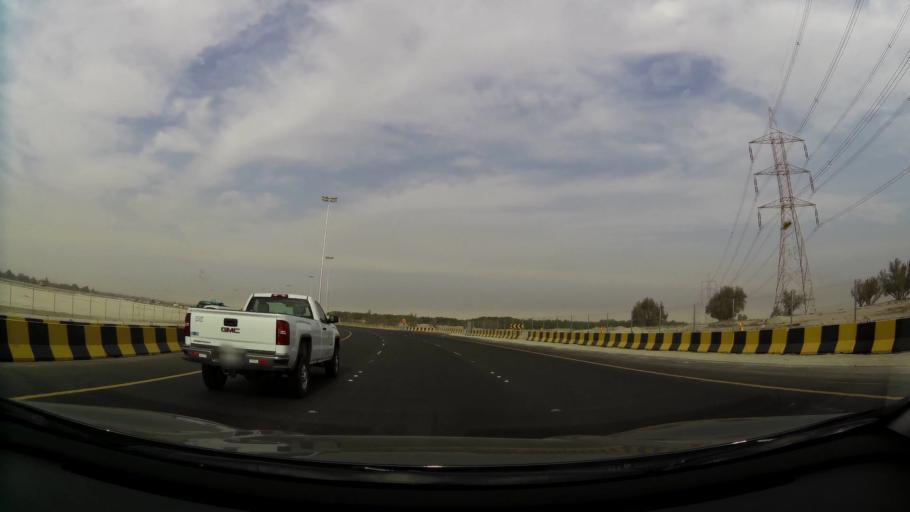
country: KW
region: Muhafazat al Jahra'
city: Al Jahra'
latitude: 29.2862
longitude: 47.7869
